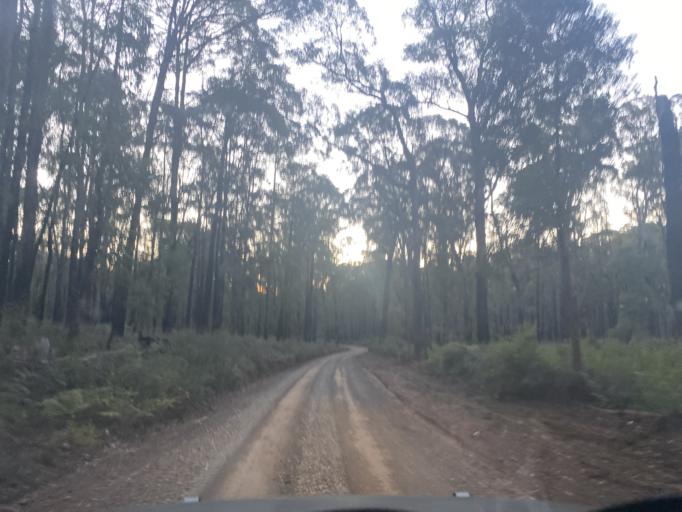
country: AU
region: Victoria
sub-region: Yarra Ranges
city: Healesville
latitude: -37.4432
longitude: 145.4966
